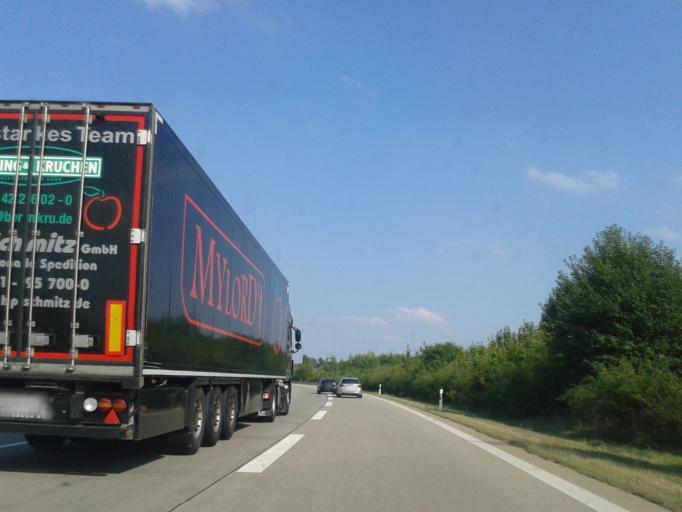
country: DE
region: Saxony
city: Freital
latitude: 51.0371
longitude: 13.6157
